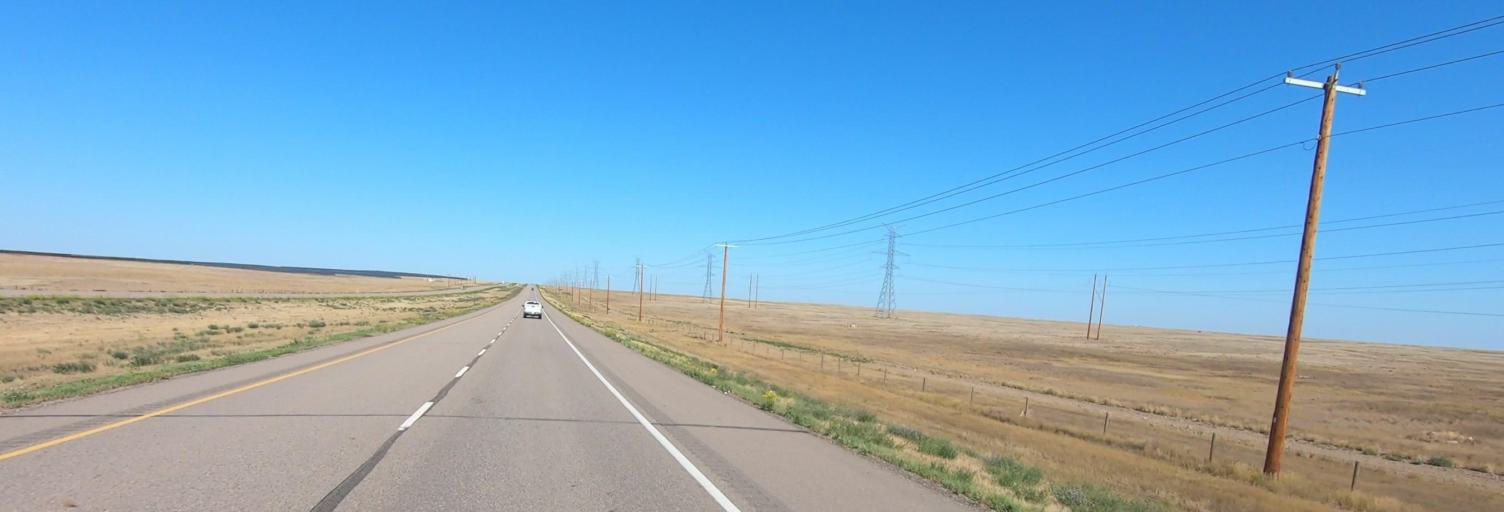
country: CA
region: Alberta
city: Bow Island
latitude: 50.2646
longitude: -111.2541
